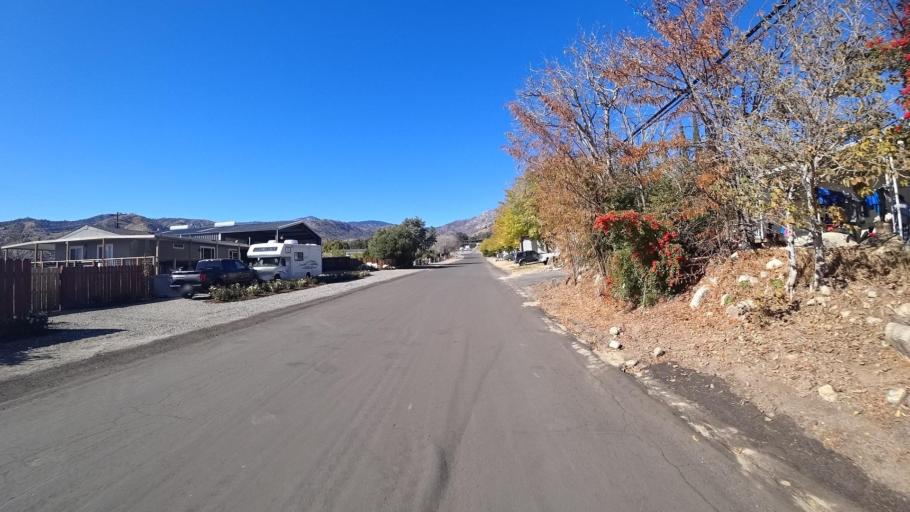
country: US
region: California
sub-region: Kern County
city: Wofford Heights
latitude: 35.7063
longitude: -118.4540
